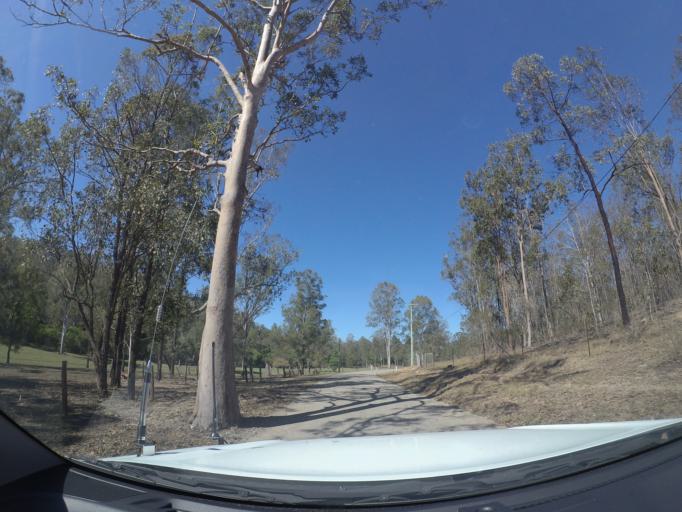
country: AU
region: Queensland
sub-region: Ipswich
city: Springfield Lakes
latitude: -27.7497
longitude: 152.8957
